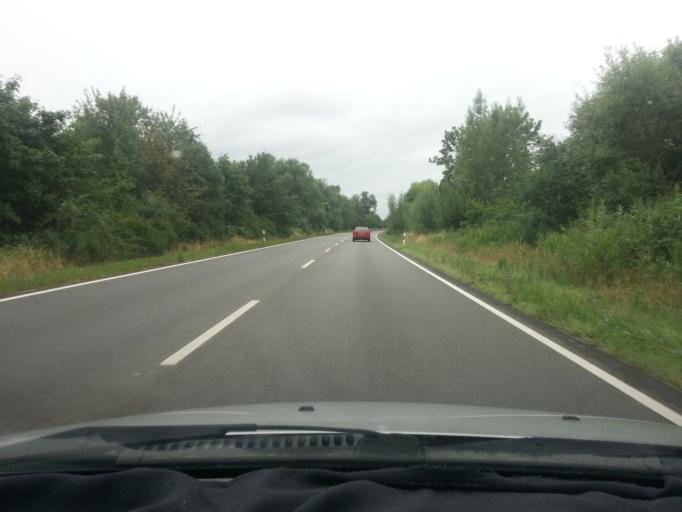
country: DE
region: Rheinland-Pfalz
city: Niederkirchen bei Deidesheim
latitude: 49.4284
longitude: 8.2032
